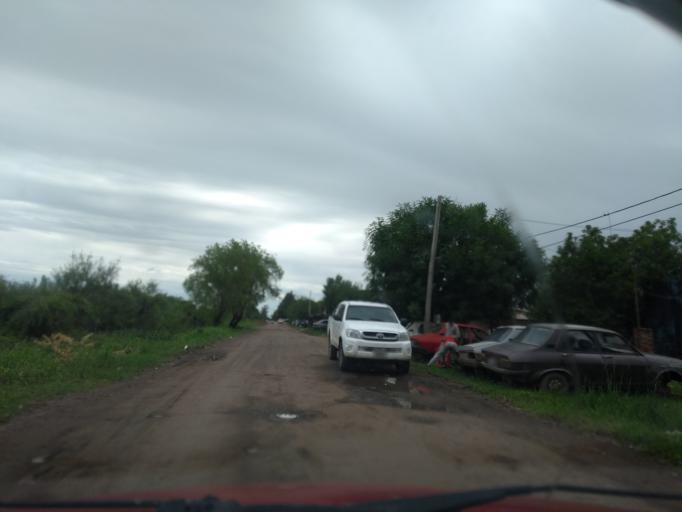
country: AR
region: Chaco
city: Barranqueras
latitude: -27.4815
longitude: -58.9632
